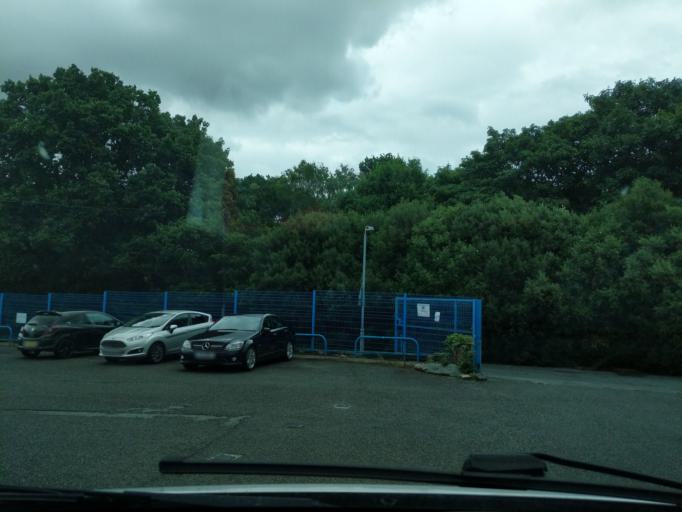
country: GB
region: England
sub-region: Cheshire West and Chester
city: Oakmere
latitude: 53.2149
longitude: -2.6487
